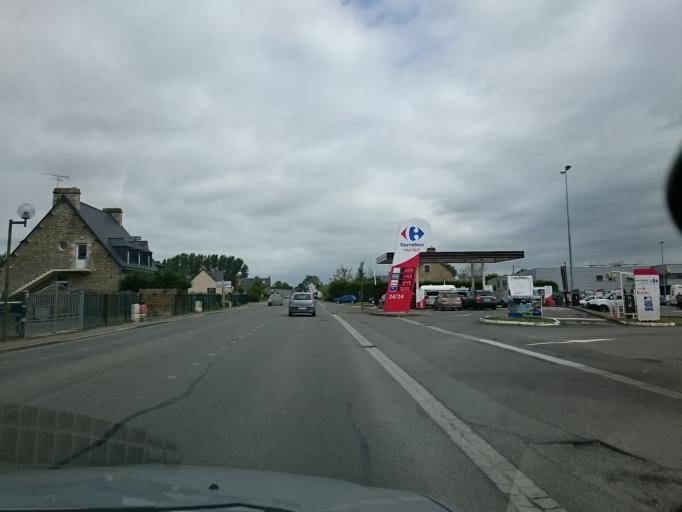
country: FR
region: Lower Normandy
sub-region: Departement de la Manche
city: Pontorson
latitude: 48.5583
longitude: -1.5093
